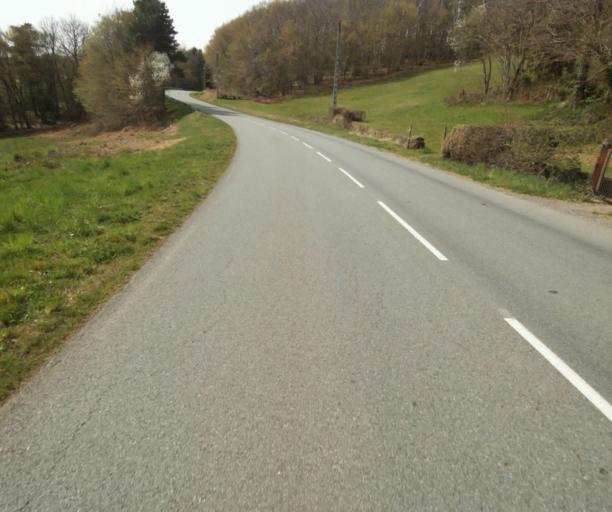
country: FR
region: Limousin
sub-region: Departement de la Correze
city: Naves
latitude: 45.3352
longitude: 1.7771
